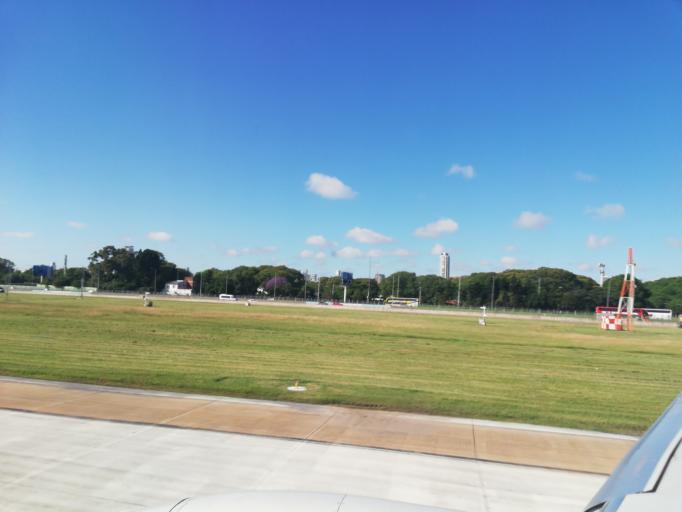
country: AR
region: Buenos Aires F.D.
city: Colegiales
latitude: -34.5556
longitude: -58.4224
